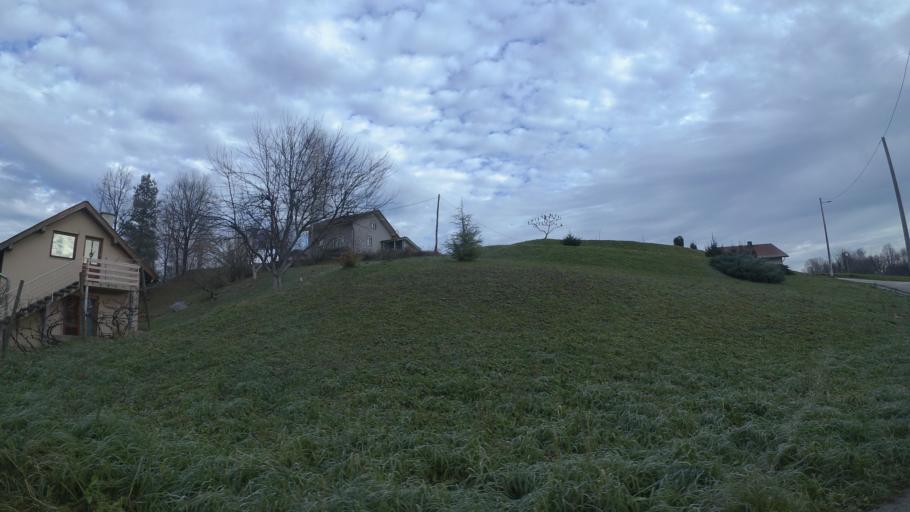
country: HR
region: Karlovacka
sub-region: Grad Karlovac
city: Karlovac
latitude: 45.4802
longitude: 15.5324
